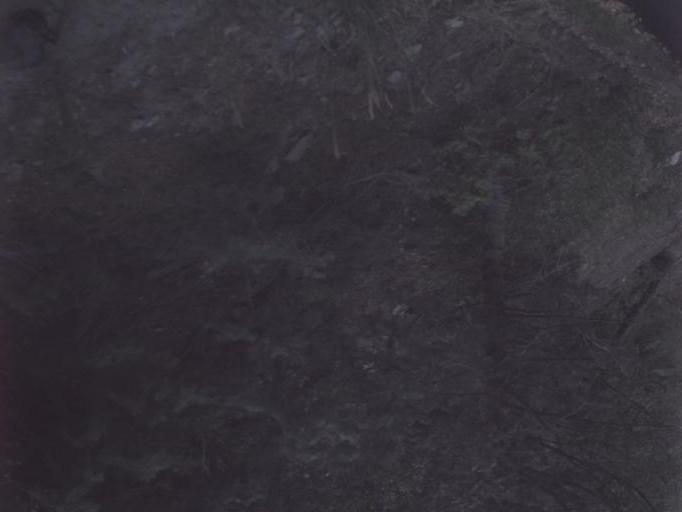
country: US
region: Utah
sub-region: Utah County
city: Cedar Hills
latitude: 40.4493
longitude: -111.6514
